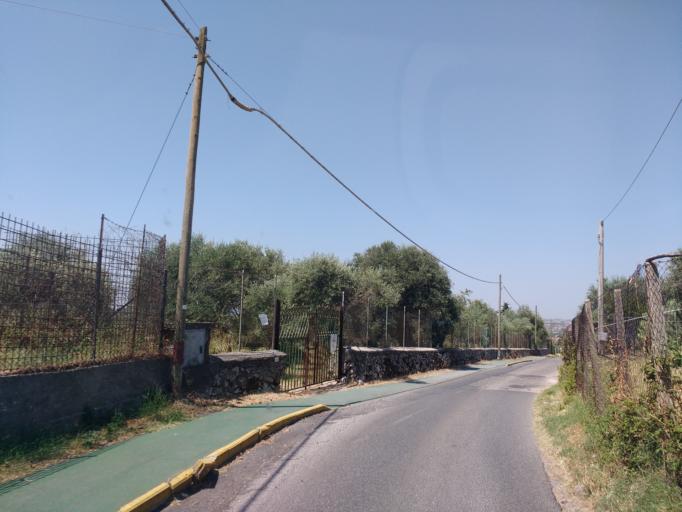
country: IT
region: Latium
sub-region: Citta metropolitana di Roma Capitale
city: Villa Adriana
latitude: 41.9474
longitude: 12.7866
